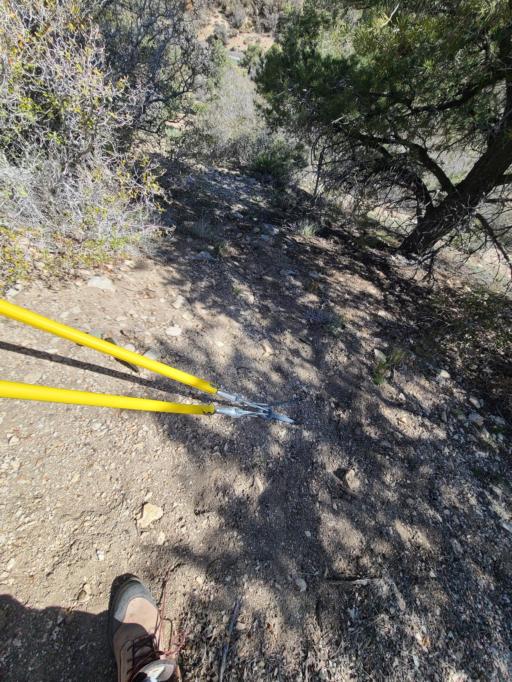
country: US
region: California
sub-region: San Bernardino County
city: Big Bear City
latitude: 34.3266
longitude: -116.8253
